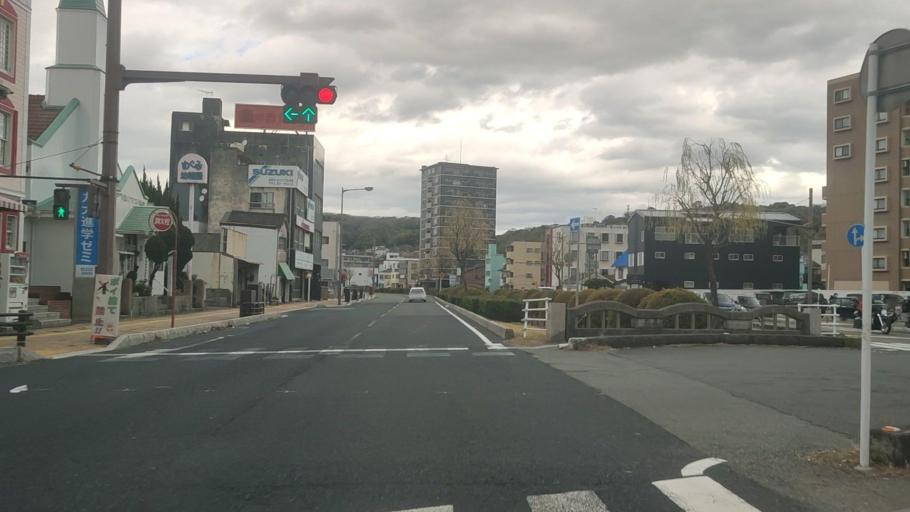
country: JP
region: Yamaguchi
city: Shimonoseki
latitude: 33.9624
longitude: 130.9418
